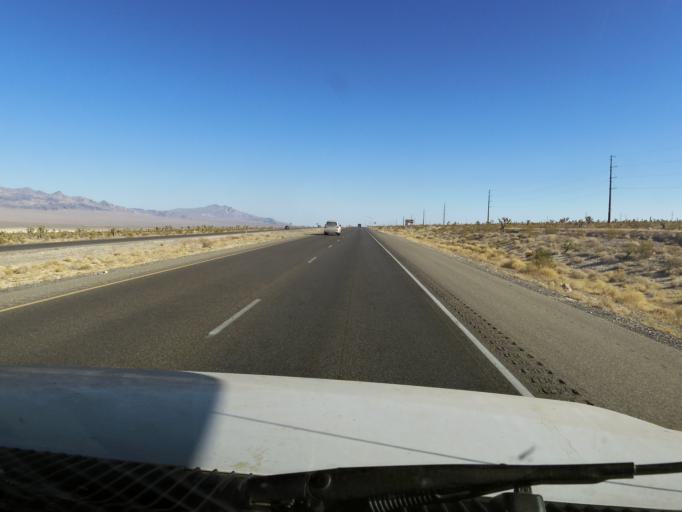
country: US
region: Nevada
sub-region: Clark County
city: Summerlin South
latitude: 36.4815
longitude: -115.4755
